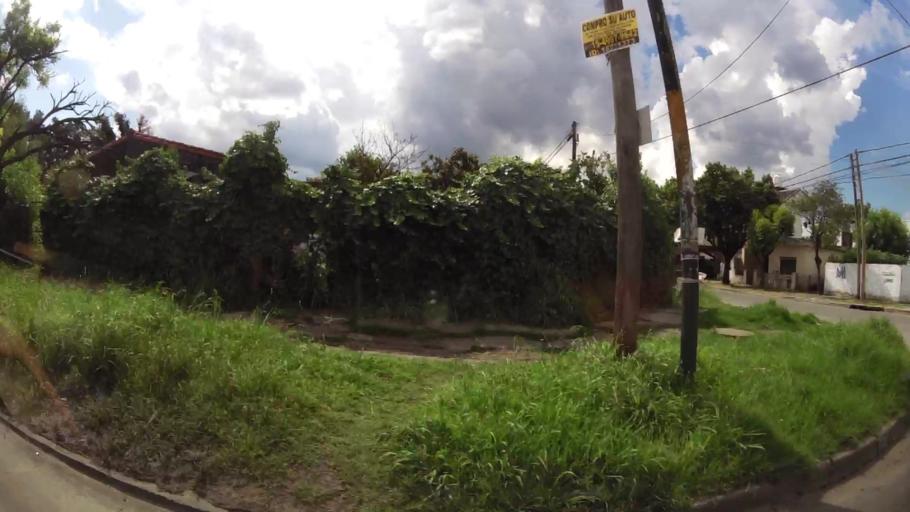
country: AR
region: Buenos Aires
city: Ituzaingo
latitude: -34.6398
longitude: -58.6731
